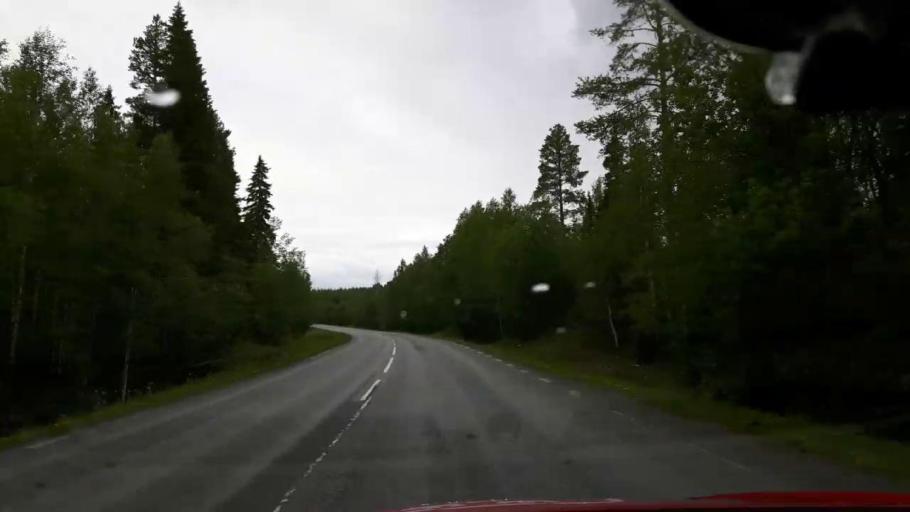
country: SE
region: Jaemtland
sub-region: Krokoms Kommun
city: Krokom
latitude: 63.4333
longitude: 14.2075
